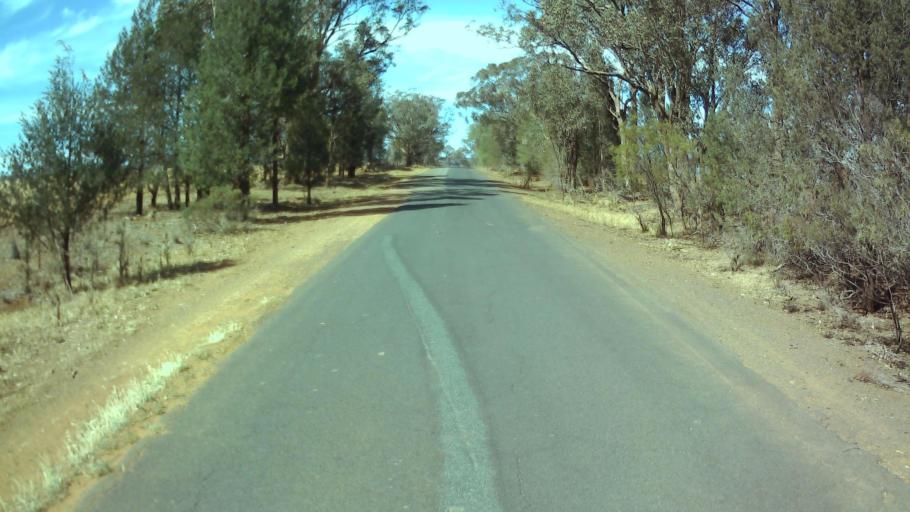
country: AU
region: New South Wales
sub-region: Weddin
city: Grenfell
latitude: -33.9331
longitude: 148.0841
